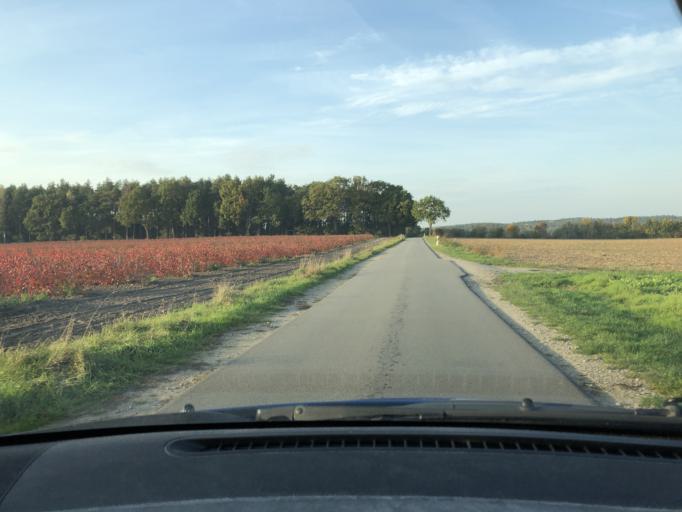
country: DE
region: Lower Saxony
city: Hitzacker
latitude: 53.1392
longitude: 11.0072
